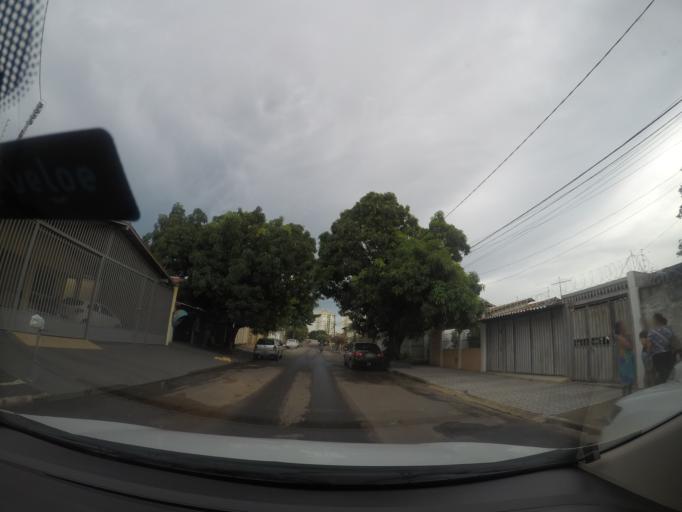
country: BR
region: Goias
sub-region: Goiania
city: Goiania
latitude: -16.6854
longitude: -49.3011
